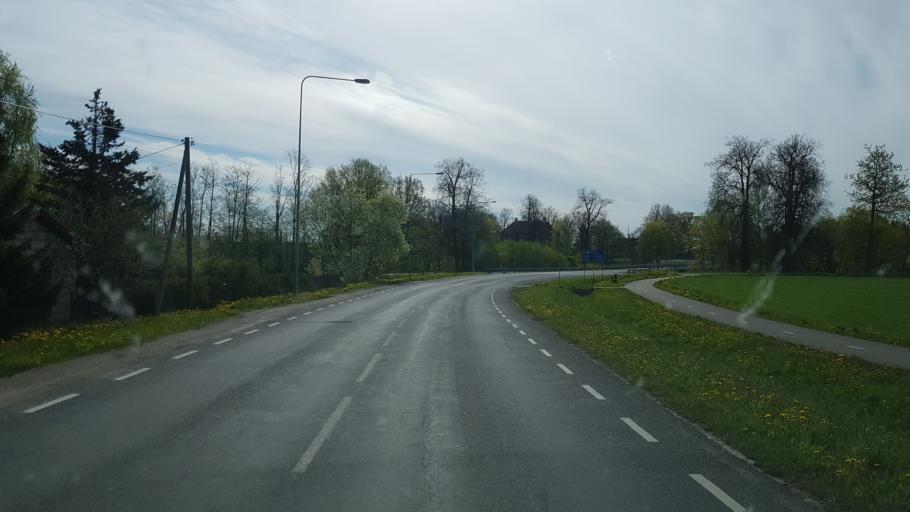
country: EE
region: Ida-Virumaa
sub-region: Kivioli linn
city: Kivioli
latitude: 59.3382
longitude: 27.0076
